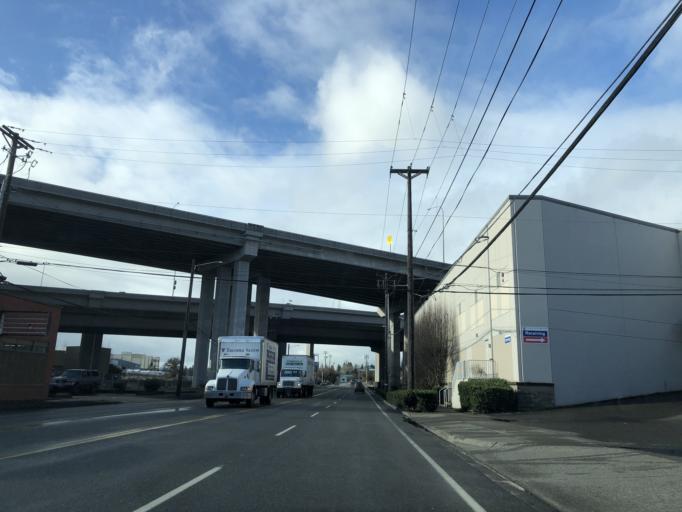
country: US
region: Washington
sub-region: Pierce County
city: Tacoma
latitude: 47.2340
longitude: -122.4617
